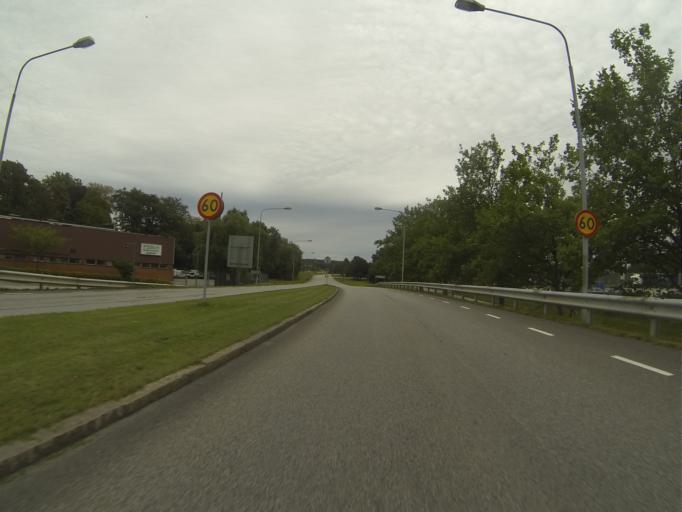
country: SE
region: Skane
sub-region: Burlovs Kommun
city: Arloev
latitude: 55.6090
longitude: 13.0634
